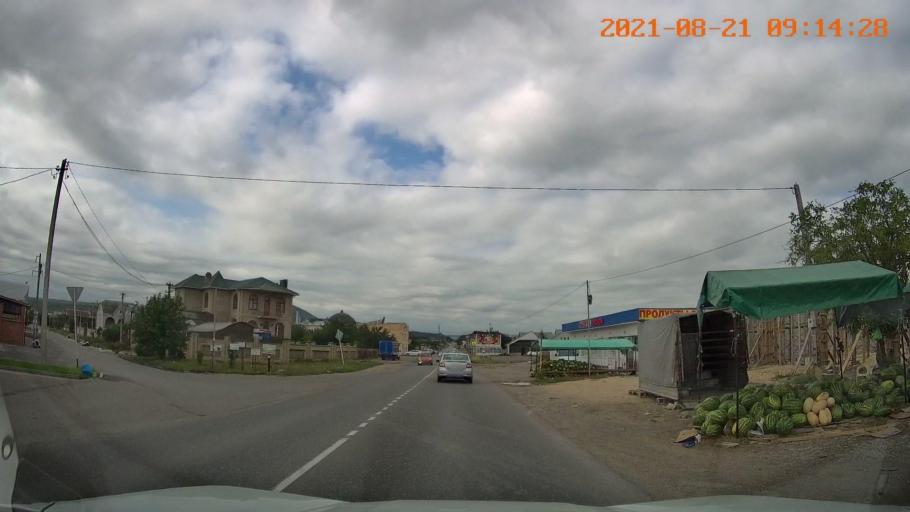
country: RU
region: Stavropol'skiy
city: Svobody
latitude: 43.9979
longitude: 43.0435
